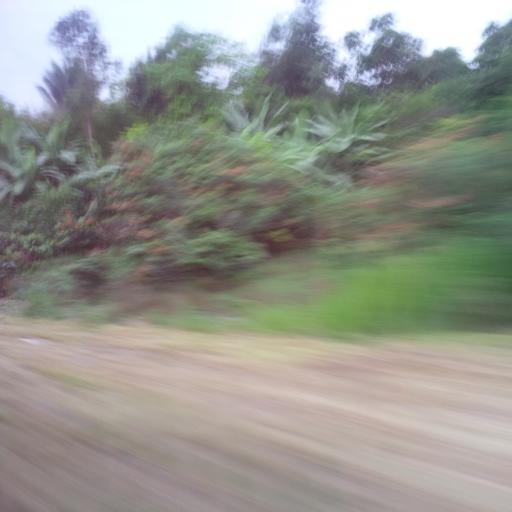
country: EC
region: Canar
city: La Troncal
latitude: -2.3204
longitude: -79.3147
